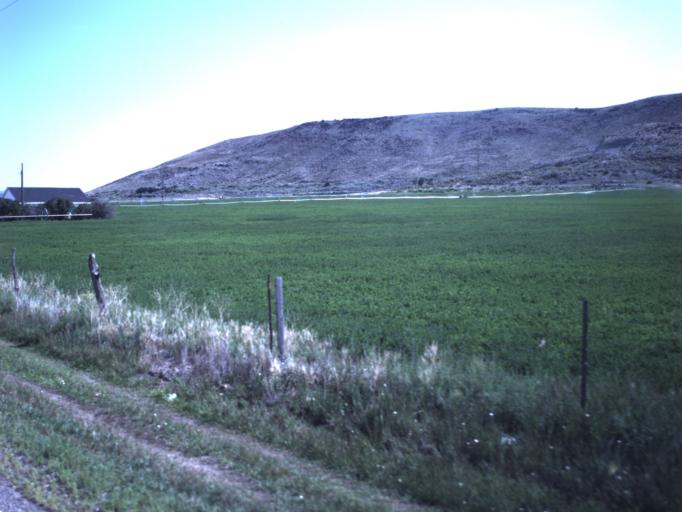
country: US
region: Utah
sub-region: Wayne County
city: Loa
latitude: 38.4225
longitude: -111.6202
